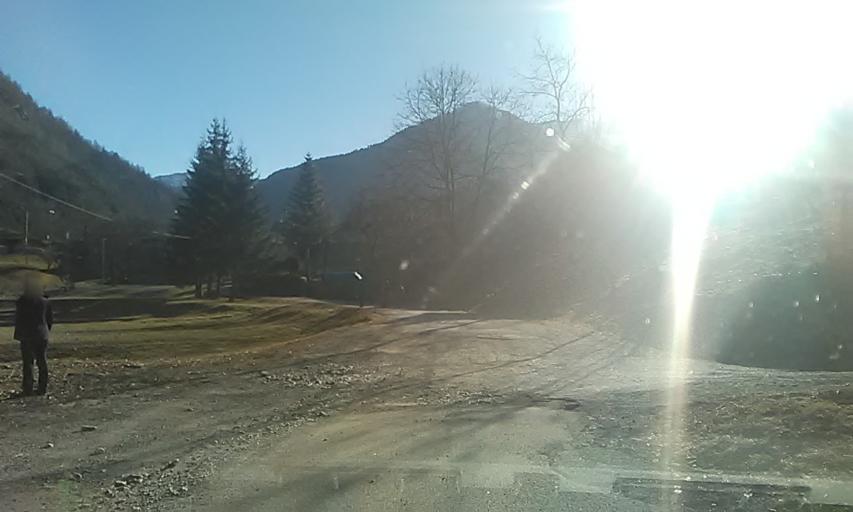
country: IT
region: Piedmont
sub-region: Provincia di Vercelli
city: Piode
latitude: 45.7813
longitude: 8.0402
